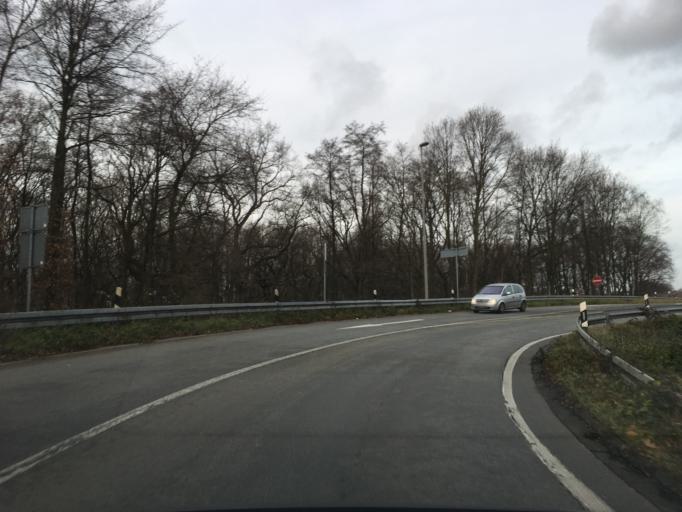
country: DE
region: North Rhine-Westphalia
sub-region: Regierungsbezirk Dusseldorf
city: Oberhausen
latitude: 51.5012
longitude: 6.8622
